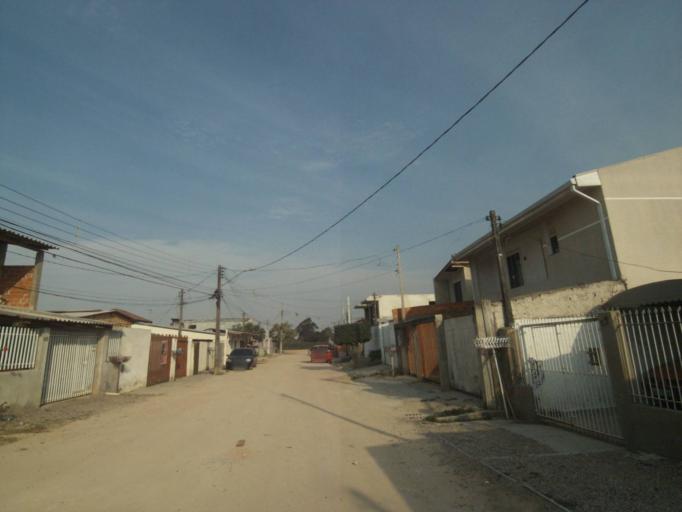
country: BR
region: Parana
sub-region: Sao Jose Dos Pinhais
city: Sao Jose dos Pinhais
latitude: -25.4980
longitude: -49.2075
